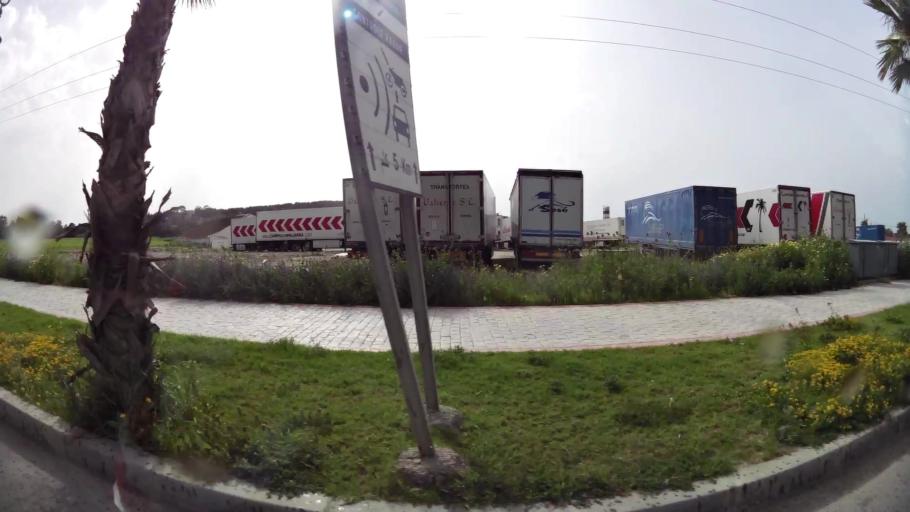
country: MA
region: Tanger-Tetouan
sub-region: Tanger-Assilah
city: Boukhalef
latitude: 35.6956
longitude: -5.9165
